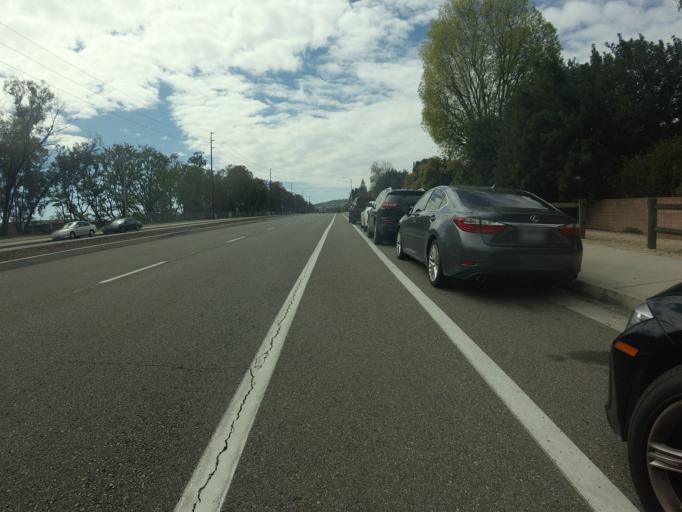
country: US
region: California
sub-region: Orange County
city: Laguna Hills
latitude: 33.5952
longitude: -117.7029
